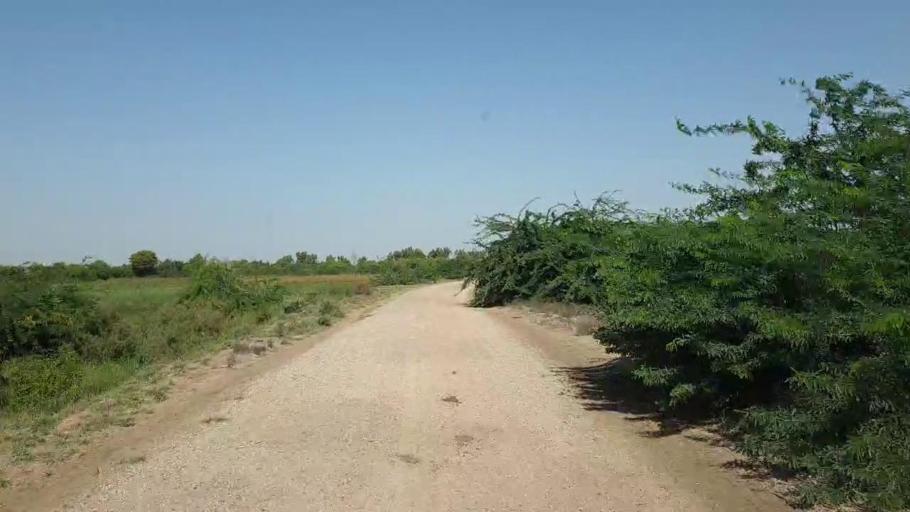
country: PK
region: Sindh
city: Tando Bago
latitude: 24.7382
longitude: 69.0431
